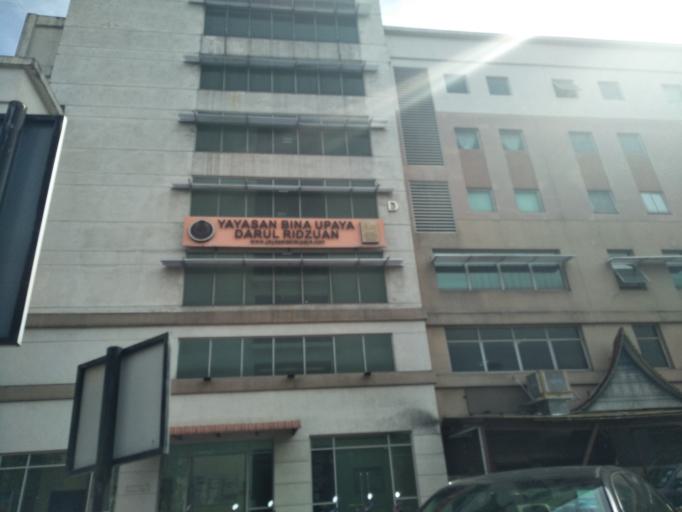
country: MY
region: Perak
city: Ipoh
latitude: 4.6005
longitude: 101.0948
